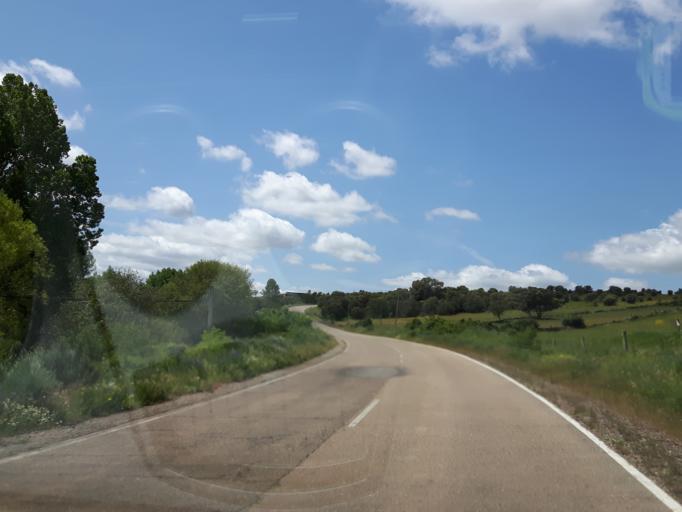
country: ES
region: Castille and Leon
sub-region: Provincia de Salamanca
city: Aldea del Obispo
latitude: 40.7166
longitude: -6.7843
